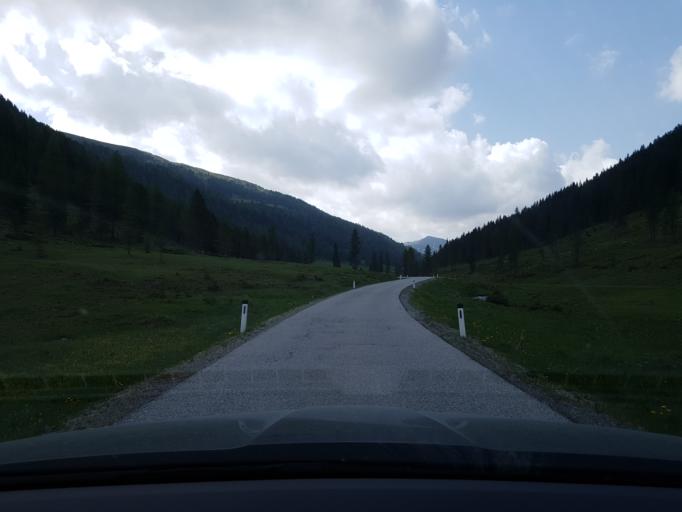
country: AT
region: Salzburg
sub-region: Politischer Bezirk Tamsweg
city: Thomatal
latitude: 47.0200
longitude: 13.7634
